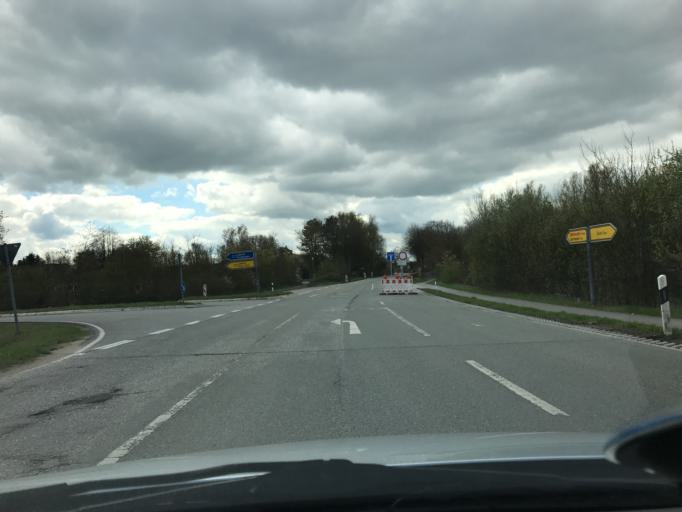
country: DE
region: Schleswig-Holstein
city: Eutin
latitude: 54.1174
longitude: 10.6129
